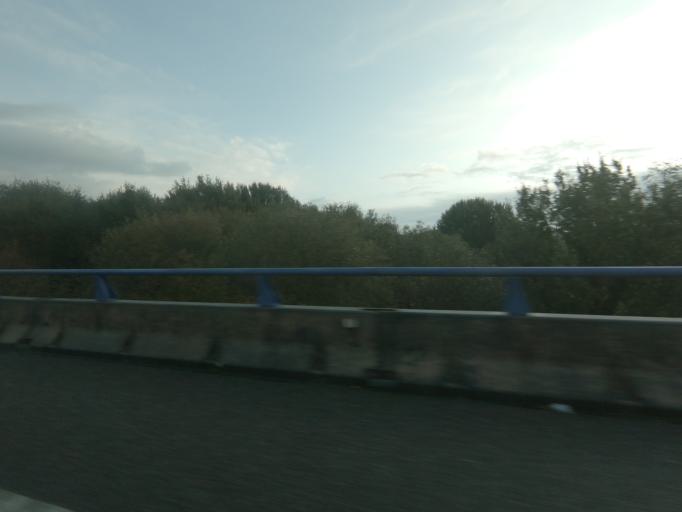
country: ES
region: Galicia
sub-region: Provincia de Pontevedra
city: Tui
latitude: 42.0962
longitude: -8.6438
